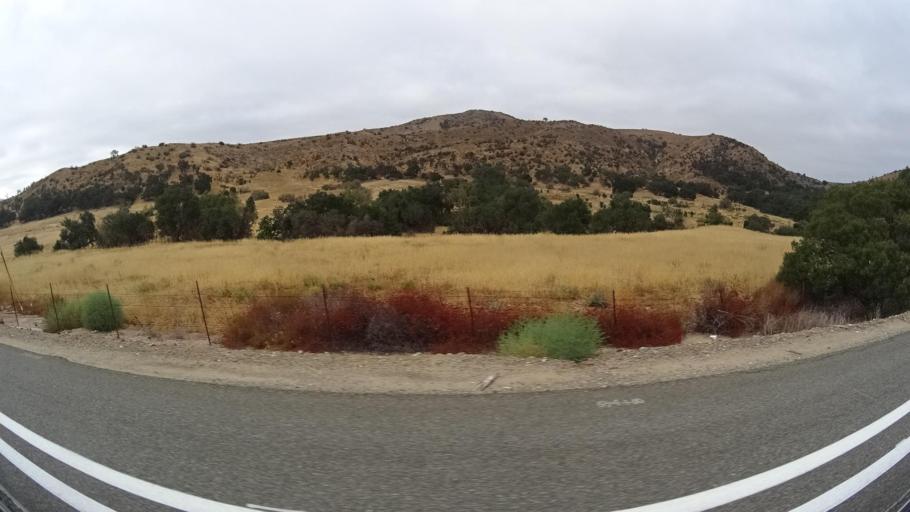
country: US
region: California
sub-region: Orange County
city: Foothill Ranch
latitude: 33.7529
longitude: -117.6907
